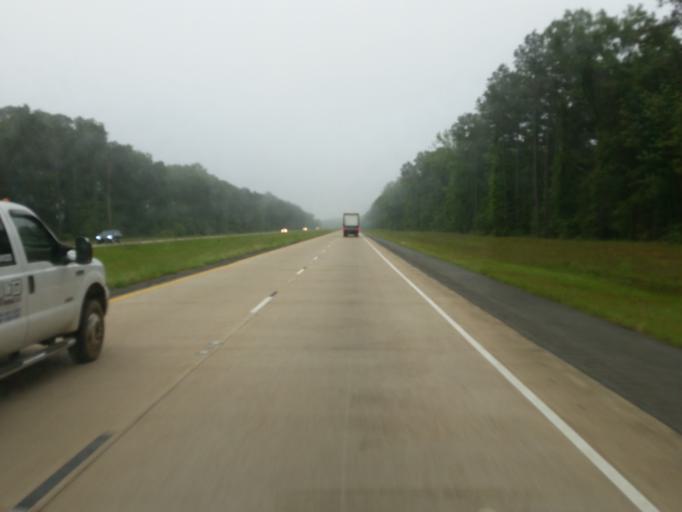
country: US
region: Louisiana
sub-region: Webster Parish
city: Sibley
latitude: 32.5855
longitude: -93.3623
